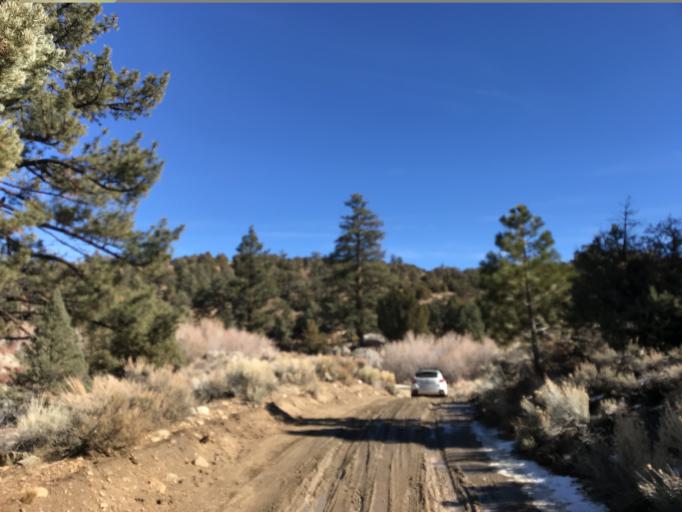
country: US
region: California
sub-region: San Bernardino County
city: Big Bear City
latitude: 34.2552
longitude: -116.7454
